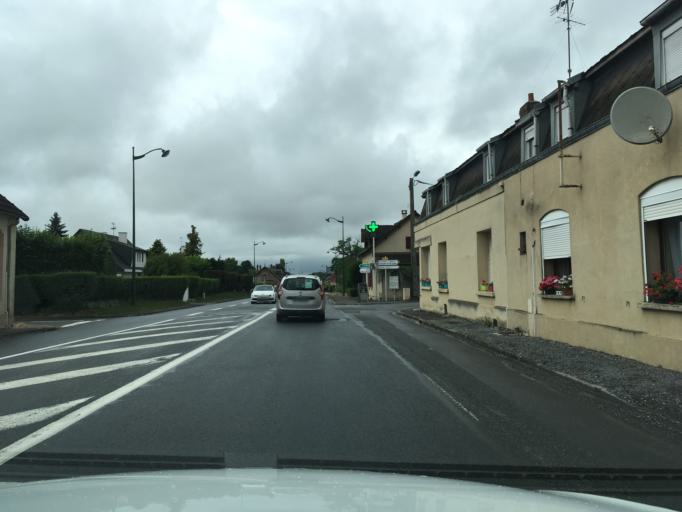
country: FR
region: Picardie
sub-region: Departement de l'Aisne
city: Homblieres
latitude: 49.8464
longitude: 3.3706
